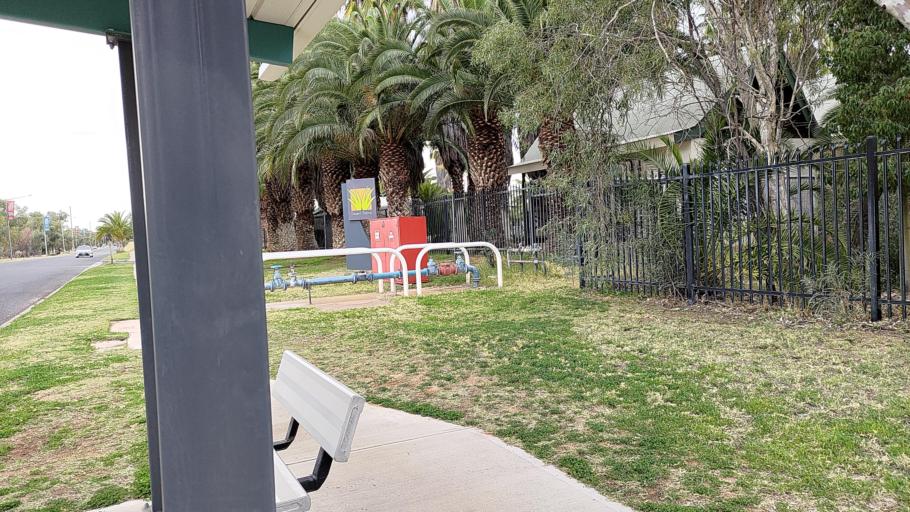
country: AU
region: Northern Territory
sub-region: Alice Springs
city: Alice Springs
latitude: -23.7139
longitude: 133.8793
